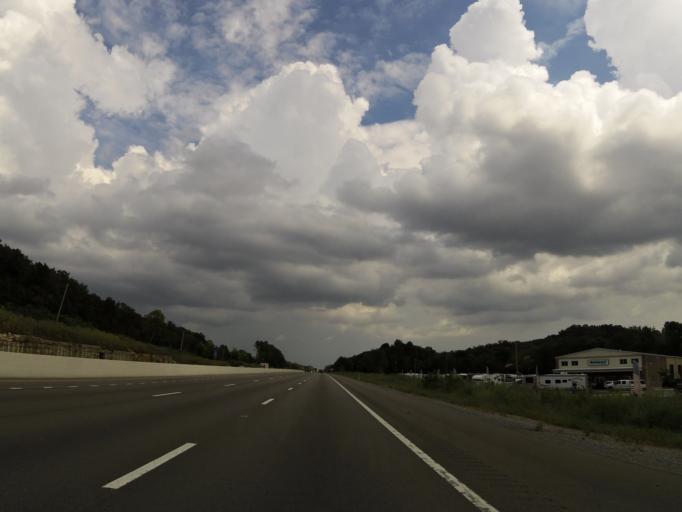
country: US
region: Tennessee
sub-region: Wilson County
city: Lebanon
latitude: 36.1847
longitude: -86.3933
